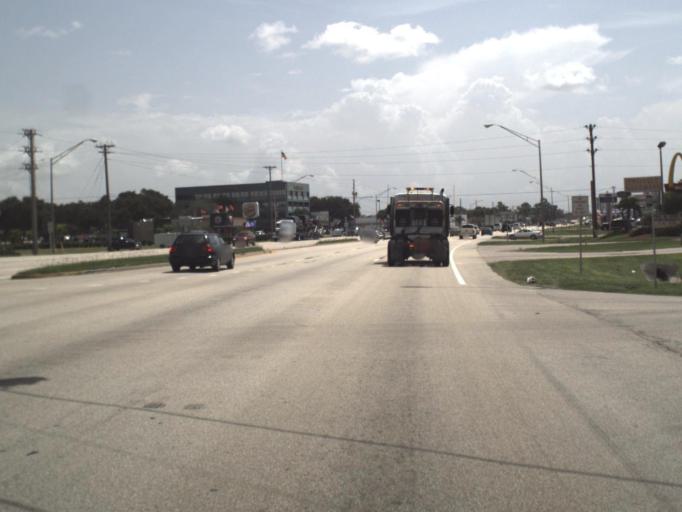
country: US
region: Florida
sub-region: Highlands County
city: Sebring
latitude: 27.4713
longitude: -81.4430
